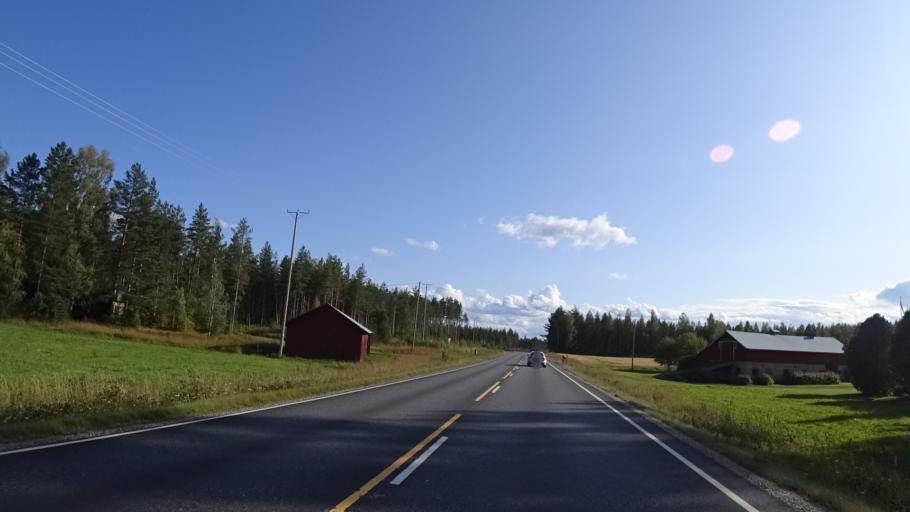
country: FI
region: North Karelia
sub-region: Keski-Karjala
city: Kesaelahti
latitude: 62.0182
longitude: 29.8898
